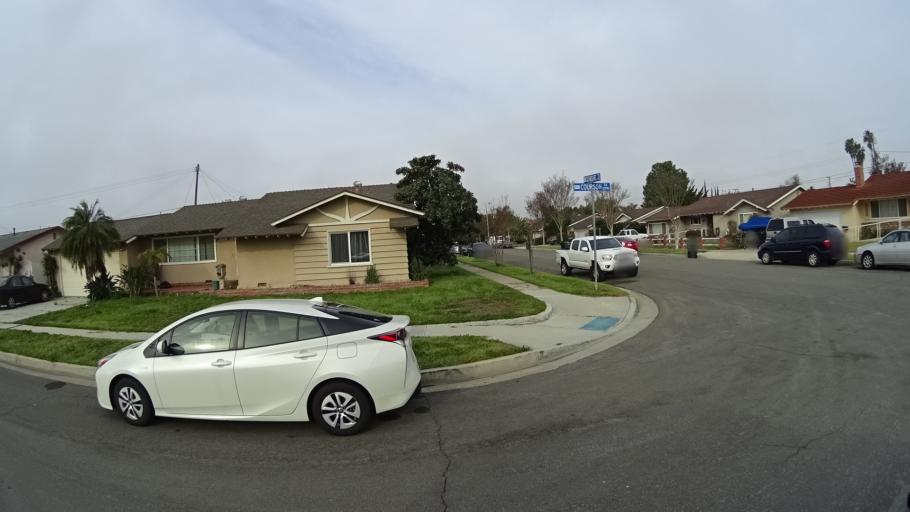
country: US
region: California
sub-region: Orange County
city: Stanton
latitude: 33.8115
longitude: -118.0043
